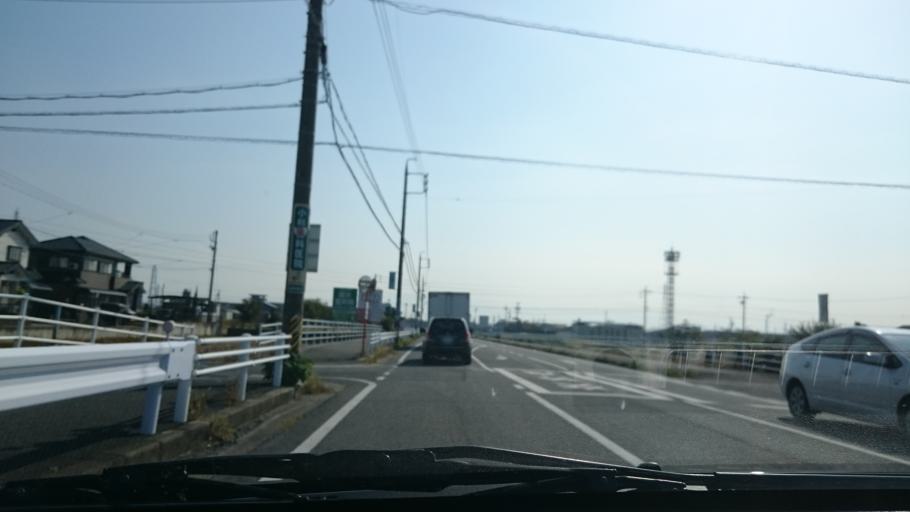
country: JP
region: Mie
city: Yokkaichi
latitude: 34.9854
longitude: 136.6169
